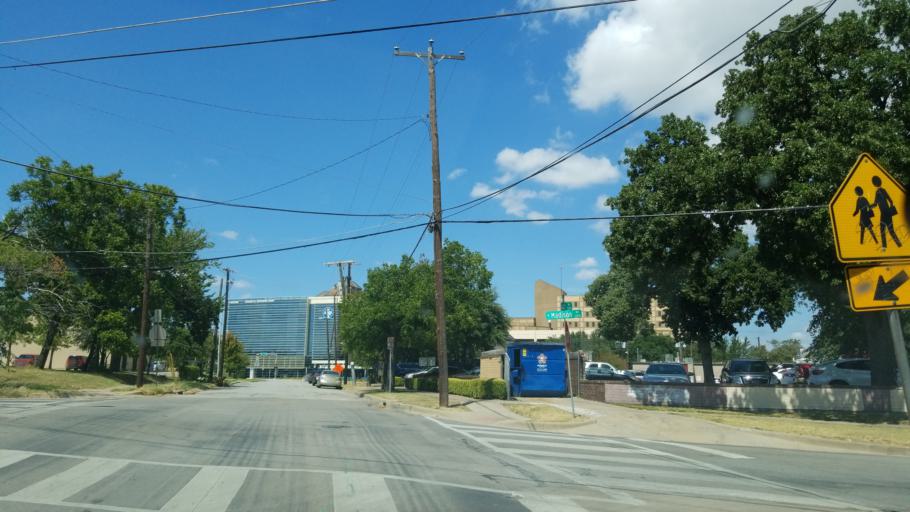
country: US
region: Texas
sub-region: Dallas County
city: Dallas
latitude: 32.7579
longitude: -96.8245
